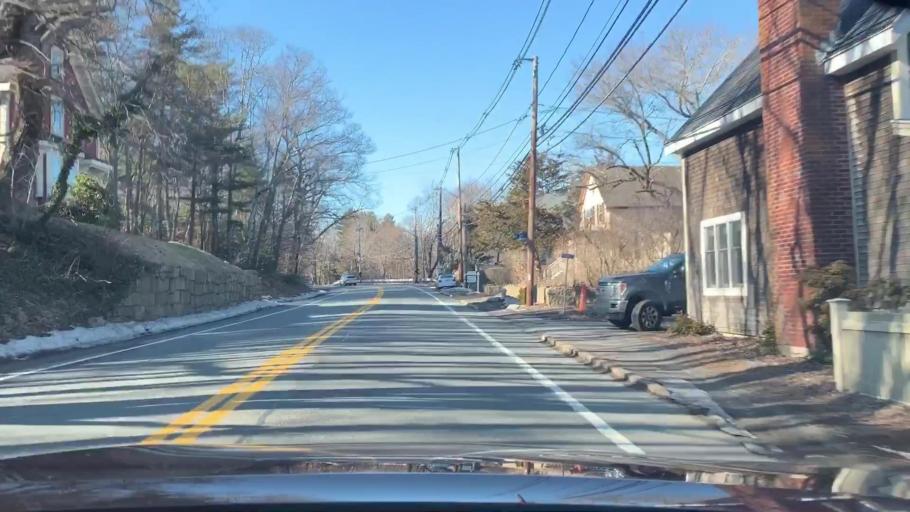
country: US
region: Massachusetts
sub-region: Essex County
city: Gloucester
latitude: 42.6148
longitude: -70.6947
